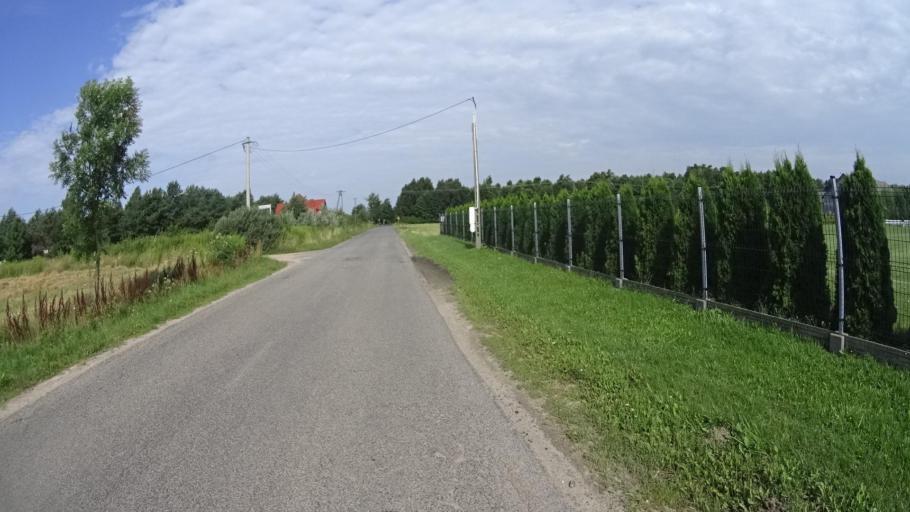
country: PL
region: Masovian Voivodeship
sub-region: Powiat piaseczynski
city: Tarczyn
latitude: 52.0100
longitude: 20.8060
